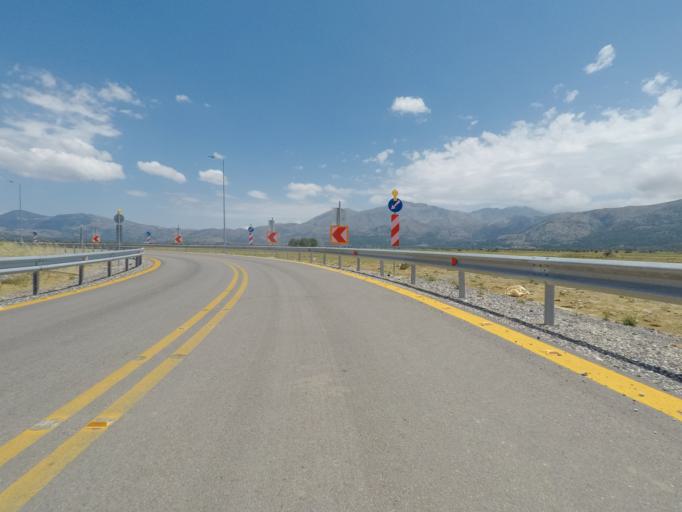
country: GR
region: Crete
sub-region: Nomos Irakleiou
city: Mokhos
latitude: 35.1943
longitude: 25.4433
